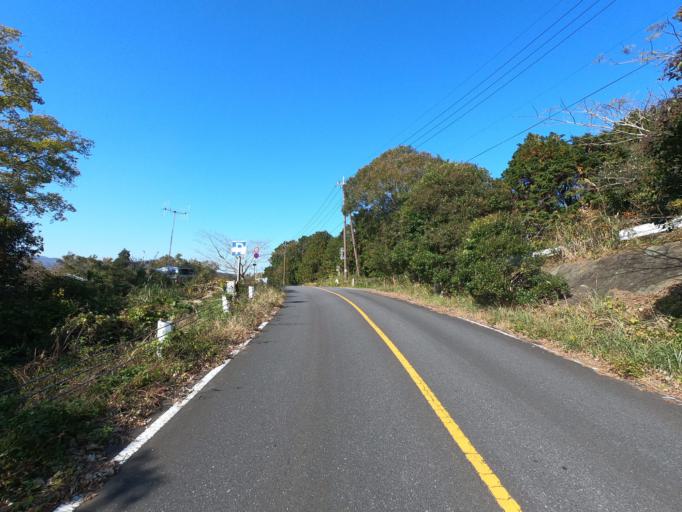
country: JP
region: Ibaraki
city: Tsukuba
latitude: 36.1709
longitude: 140.1715
